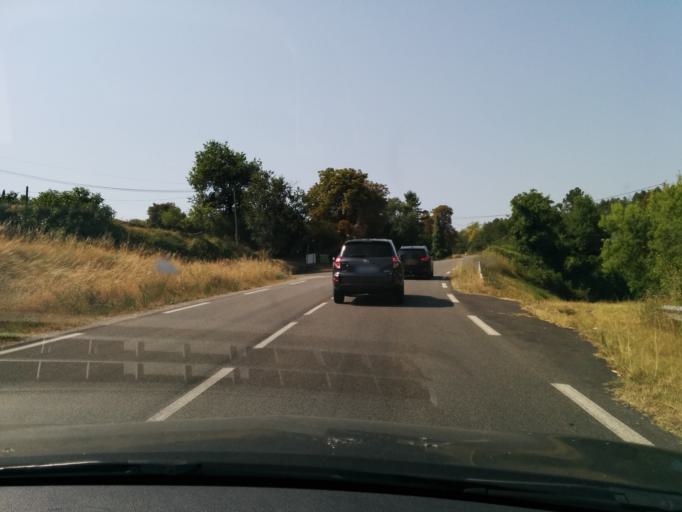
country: FR
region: Midi-Pyrenees
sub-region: Departement du Tarn
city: Castelnau-de-Levis
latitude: 43.9542
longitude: 2.1156
